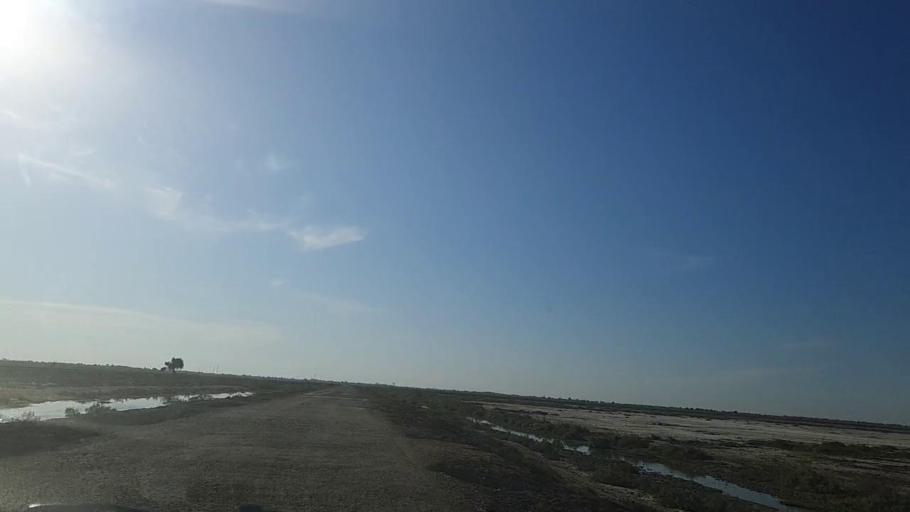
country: PK
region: Sindh
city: Pithoro
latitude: 25.5098
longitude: 69.4240
